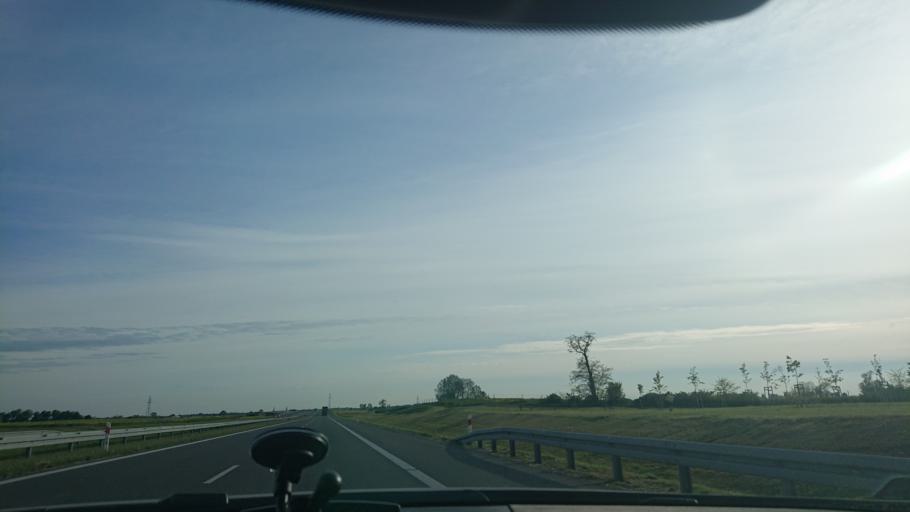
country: PL
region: Greater Poland Voivodeship
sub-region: Powiat gnieznienski
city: Gniezno
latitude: 52.5381
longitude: 17.5231
